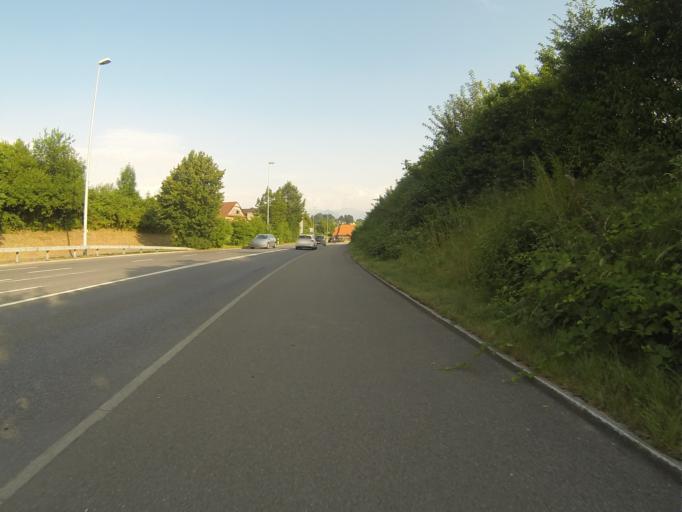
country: CH
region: Lucerne
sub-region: Lucerne-Stadt District
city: Luzern
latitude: 47.0671
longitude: 8.2961
